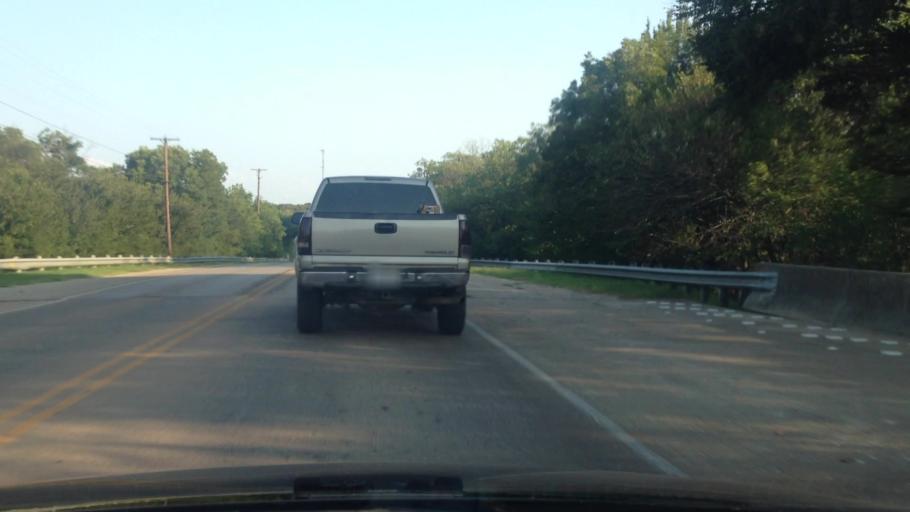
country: US
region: Texas
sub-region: Tarrant County
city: Rendon
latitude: 32.6031
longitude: -97.2649
